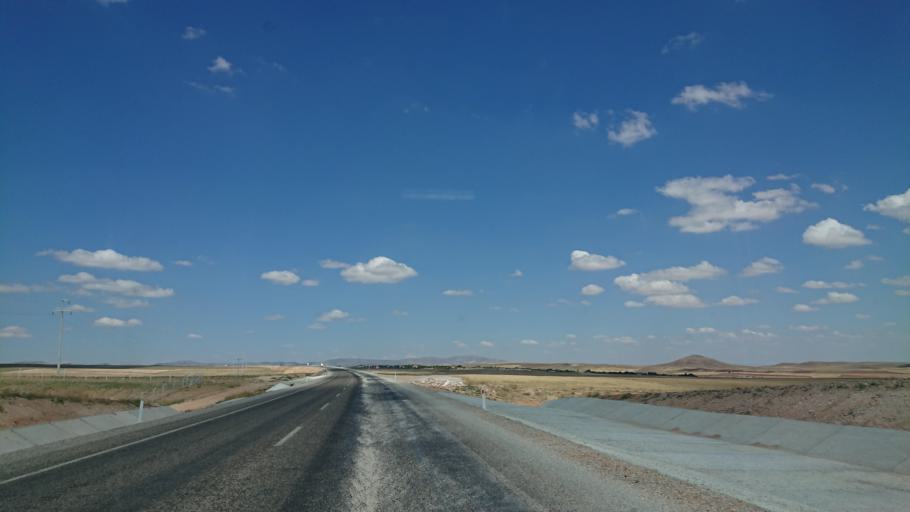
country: TR
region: Kirsehir
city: Kirsehir
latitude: 39.1221
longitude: 34.0167
